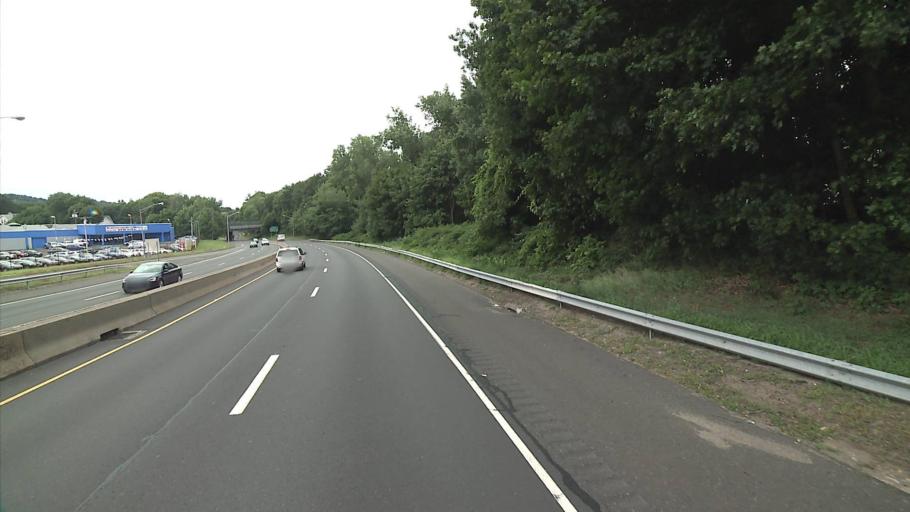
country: US
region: Connecticut
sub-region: New Haven County
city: Derby
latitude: 41.3332
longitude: -73.0921
